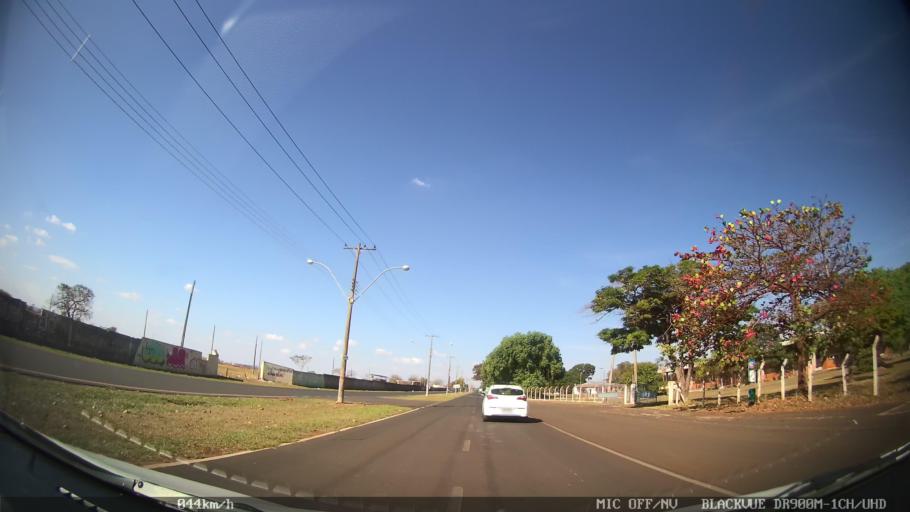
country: BR
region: Sao Paulo
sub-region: Ribeirao Preto
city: Ribeirao Preto
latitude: -21.1495
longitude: -47.7700
